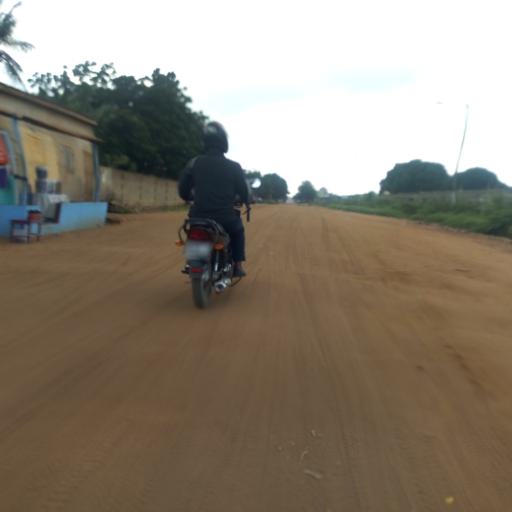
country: TG
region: Maritime
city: Lome
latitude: 6.1911
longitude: 1.2567
